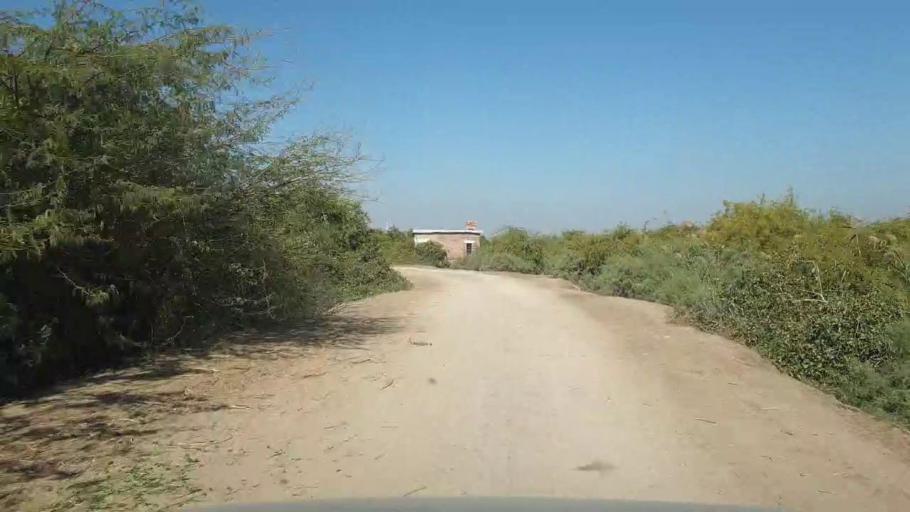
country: PK
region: Sindh
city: Mirwah Gorchani
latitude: 25.2854
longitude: 69.1024
